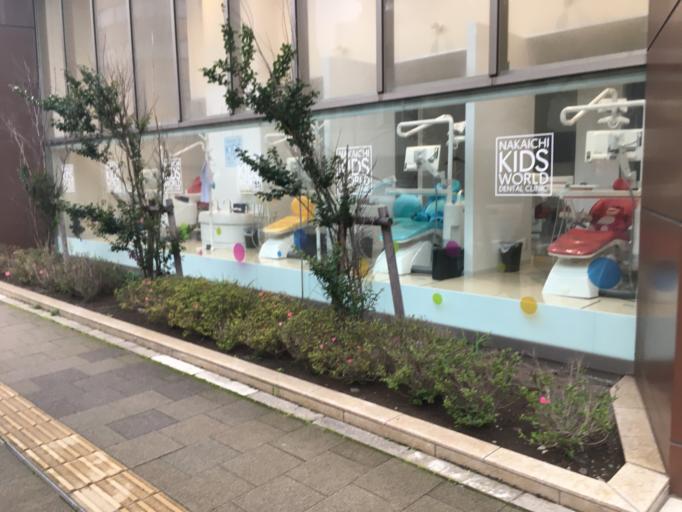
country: JP
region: Akita
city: Akita
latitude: 39.7163
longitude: 140.1213
